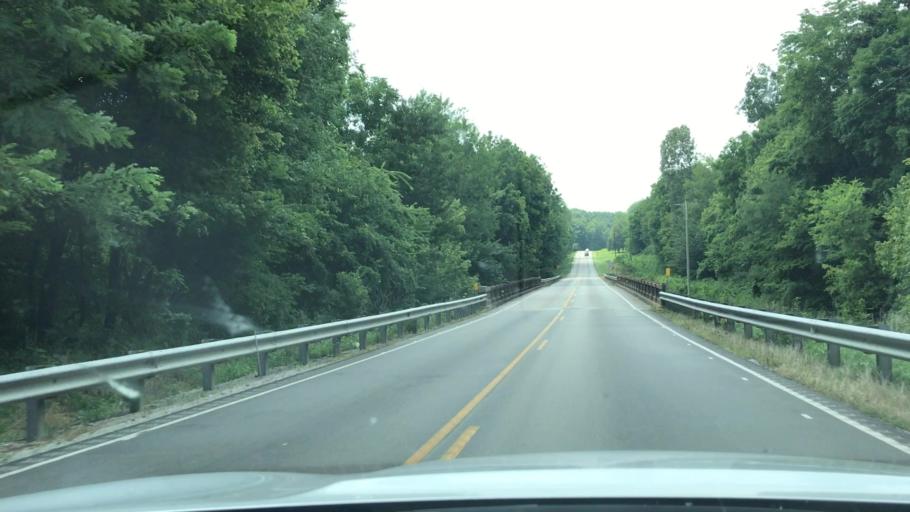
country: US
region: Kentucky
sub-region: Todd County
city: Guthrie
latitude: 36.7130
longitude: -87.0988
